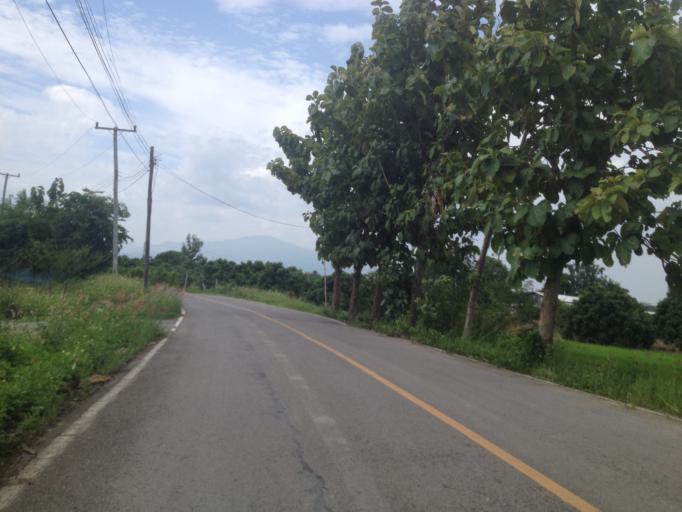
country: TH
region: Chiang Mai
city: Hang Dong
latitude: 18.6674
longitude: 98.9643
